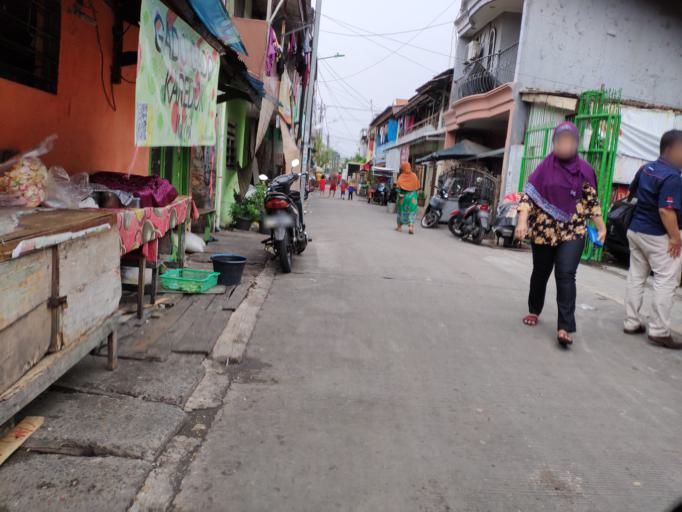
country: ID
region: Jakarta Raya
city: Jakarta
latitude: -6.1988
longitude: 106.8571
